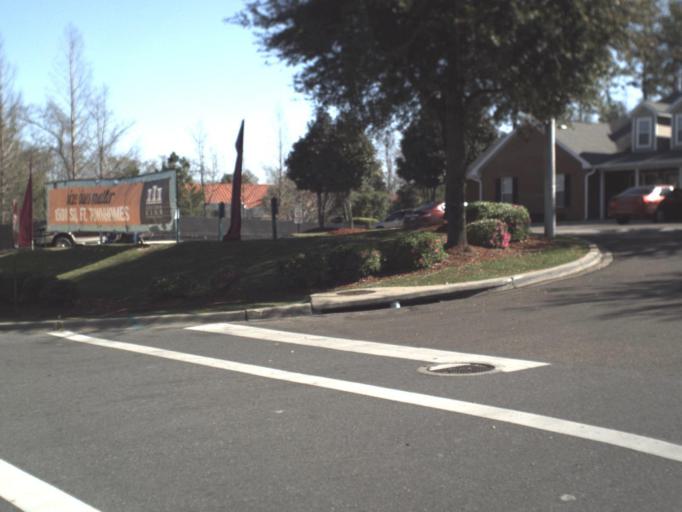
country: US
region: Florida
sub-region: Leon County
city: Tallahassee
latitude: 30.4096
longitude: -84.2834
